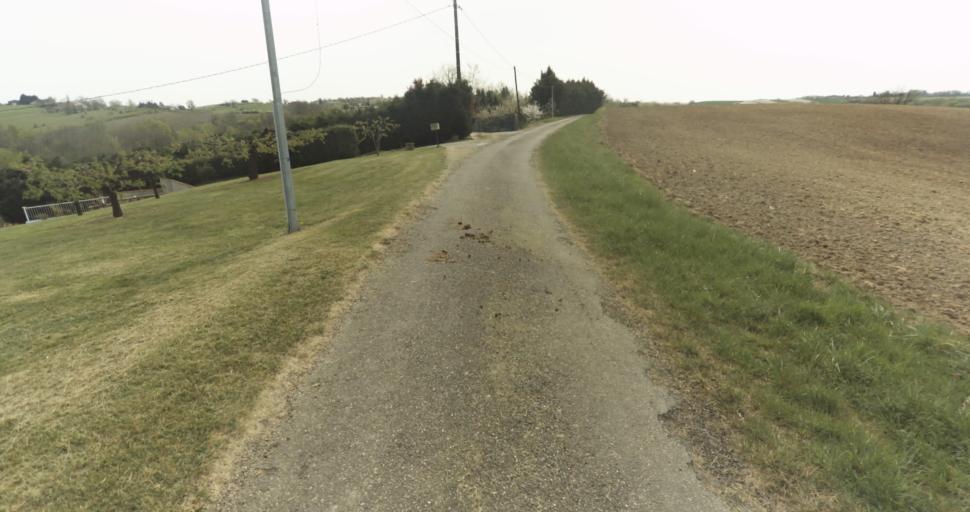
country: FR
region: Midi-Pyrenees
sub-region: Departement du Tarn-et-Garonne
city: Moissac
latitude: 44.1144
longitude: 1.0541
